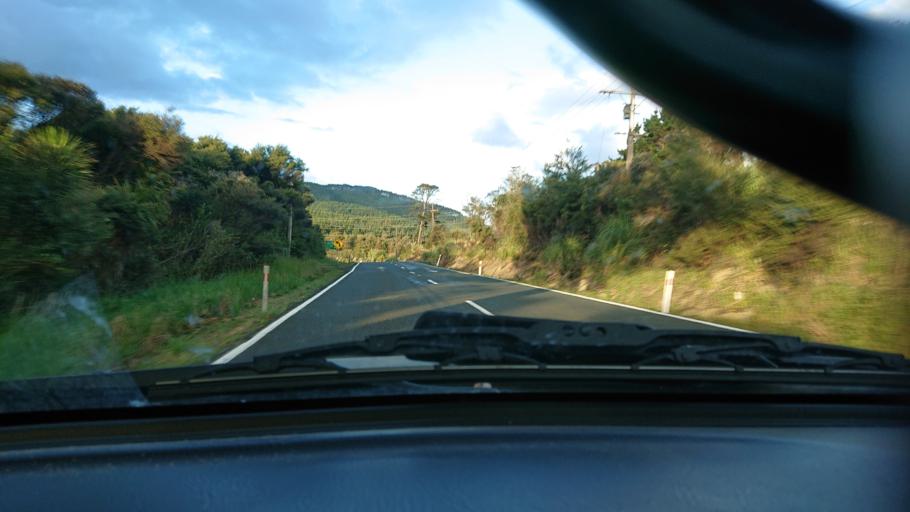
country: NZ
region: Auckland
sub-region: Auckland
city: Parakai
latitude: -36.5093
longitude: 174.4554
